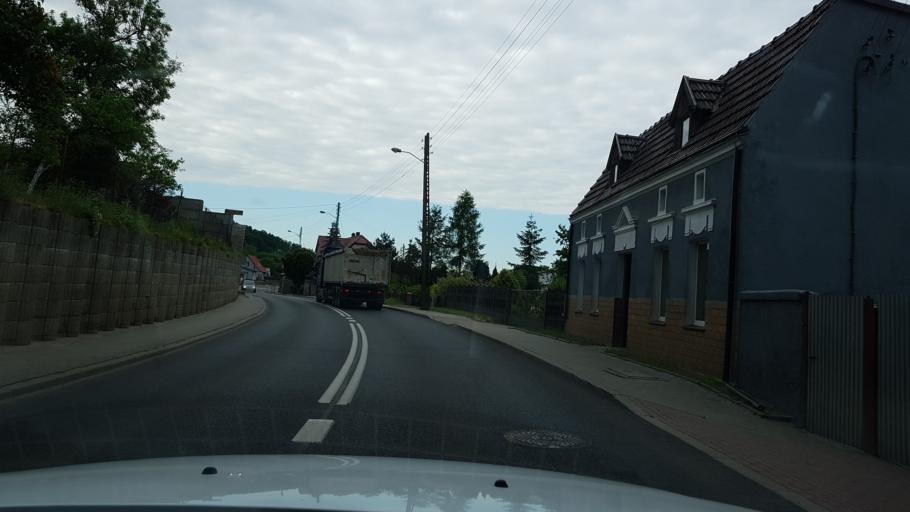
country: PL
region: West Pomeranian Voivodeship
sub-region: Powiat gryfinski
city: Gryfino
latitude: 53.2828
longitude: 14.5144
